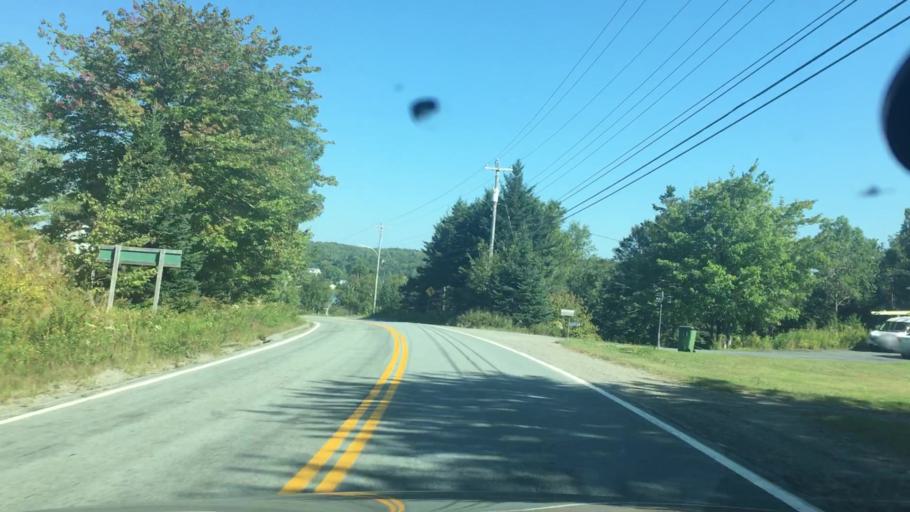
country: CA
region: Nova Scotia
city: New Glasgow
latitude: 44.9144
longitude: -62.5388
